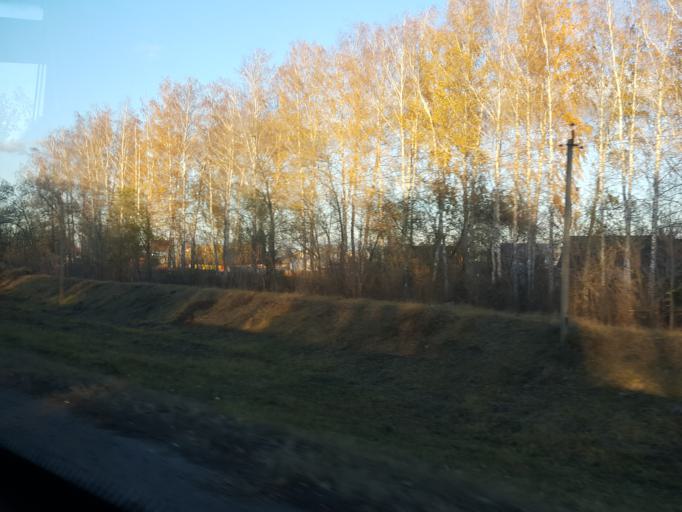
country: RU
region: Tambov
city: Bokino
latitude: 52.6214
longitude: 41.4439
